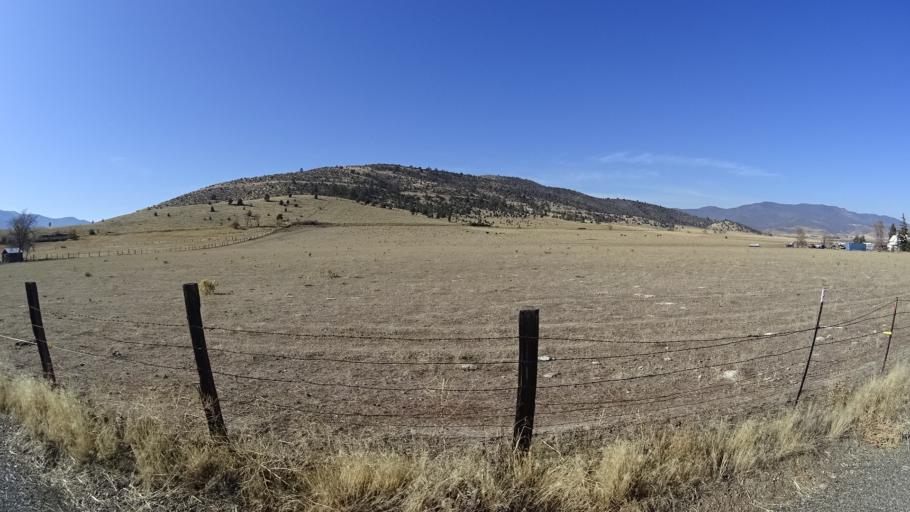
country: US
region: California
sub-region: Siskiyou County
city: Weed
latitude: 41.5161
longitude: -122.5255
